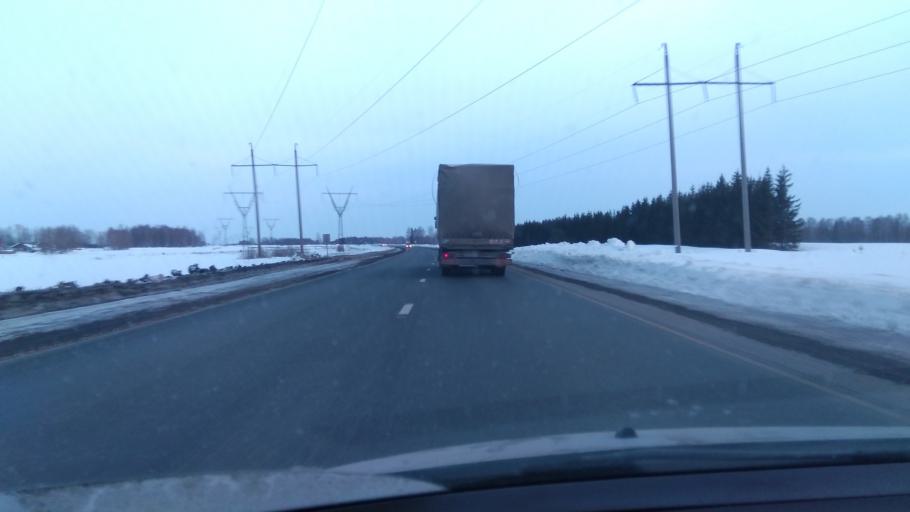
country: RU
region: Perm
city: Orda
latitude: 57.2625
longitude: 57.0240
